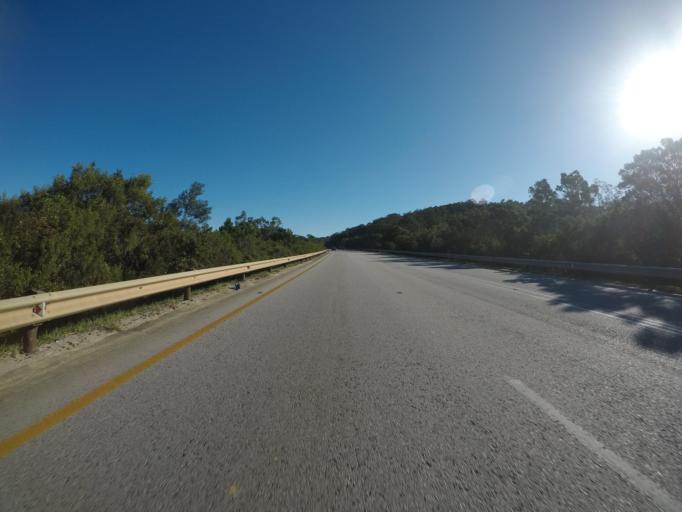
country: ZA
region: Eastern Cape
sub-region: Cacadu District Municipality
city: Jeffrey's Bay
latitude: -33.9022
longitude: 25.0849
